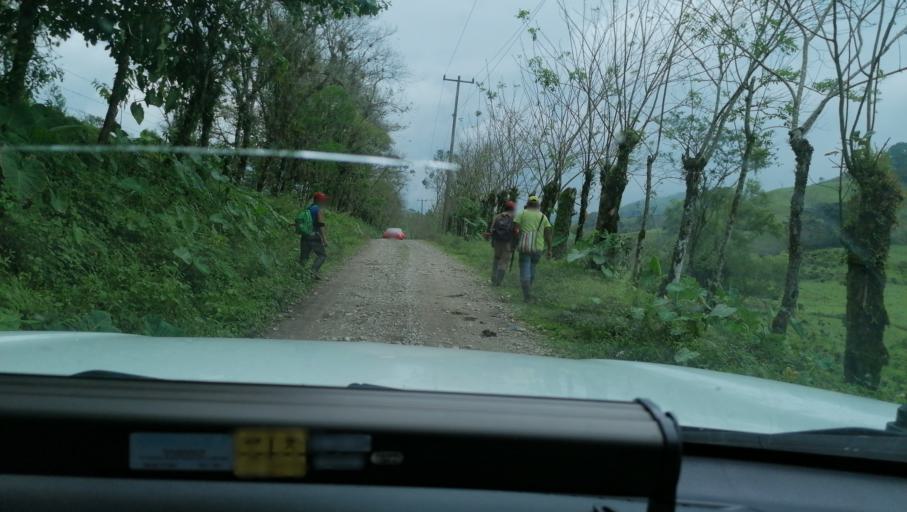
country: MX
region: Chiapas
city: Ixtacomitan
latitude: 17.3515
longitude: -93.1587
